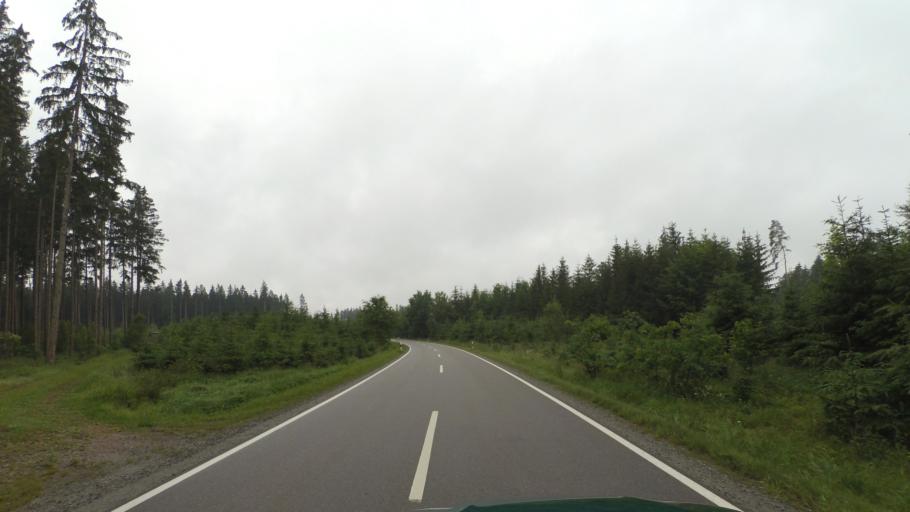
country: DE
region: Bavaria
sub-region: Lower Bavaria
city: Mallersdorf-Pfaffenberg
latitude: 48.8003
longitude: 12.2380
